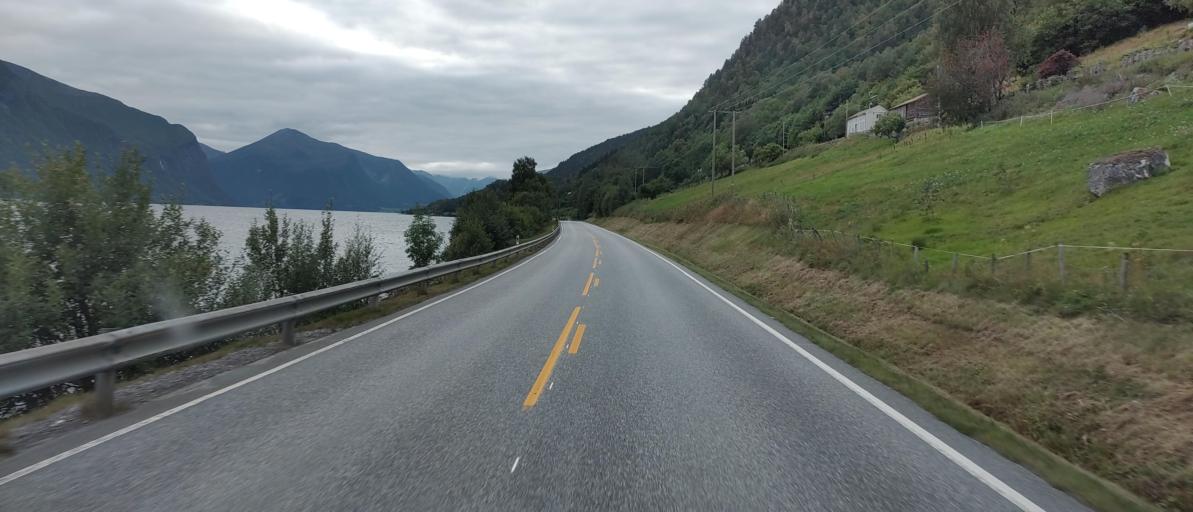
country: NO
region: More og Romsdal
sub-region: Rauma
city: Andalsnes
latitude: 62.5808
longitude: 7.6908
